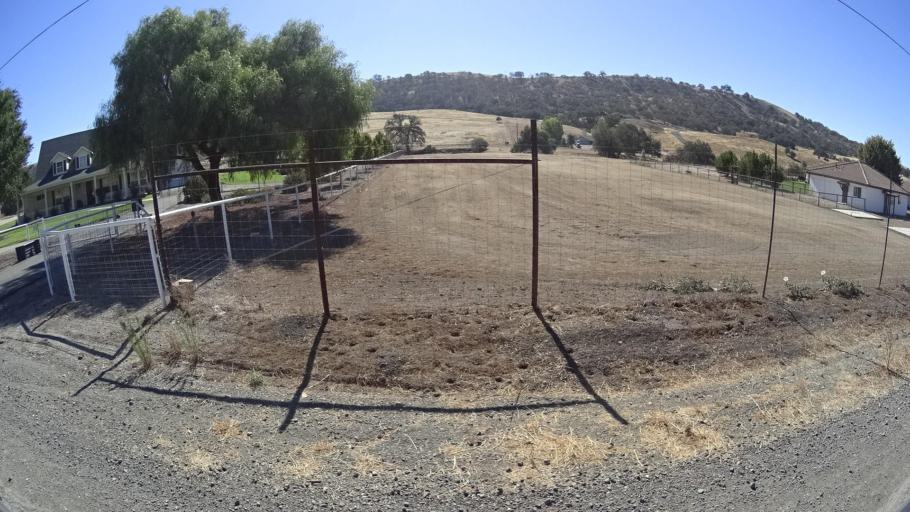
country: US
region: California
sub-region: San Luis Obispo County
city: San Miguel
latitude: 35.7929
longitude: -120.5772
